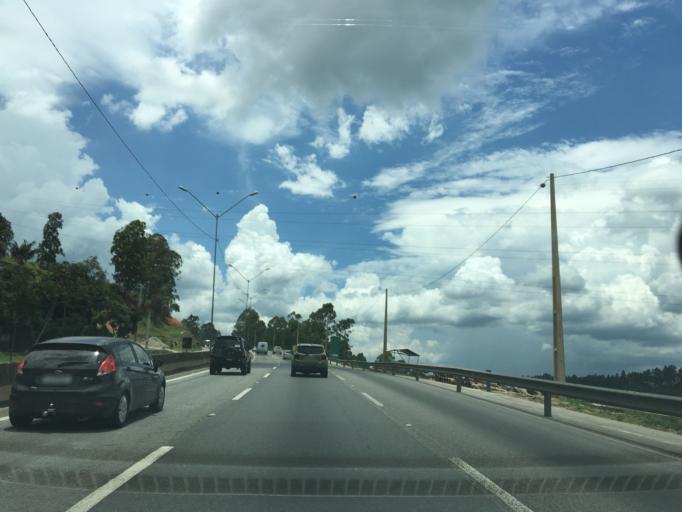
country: BR
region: Sao Paulo
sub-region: Mairipora
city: Mairipora
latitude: -23.3065
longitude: -46.5757
